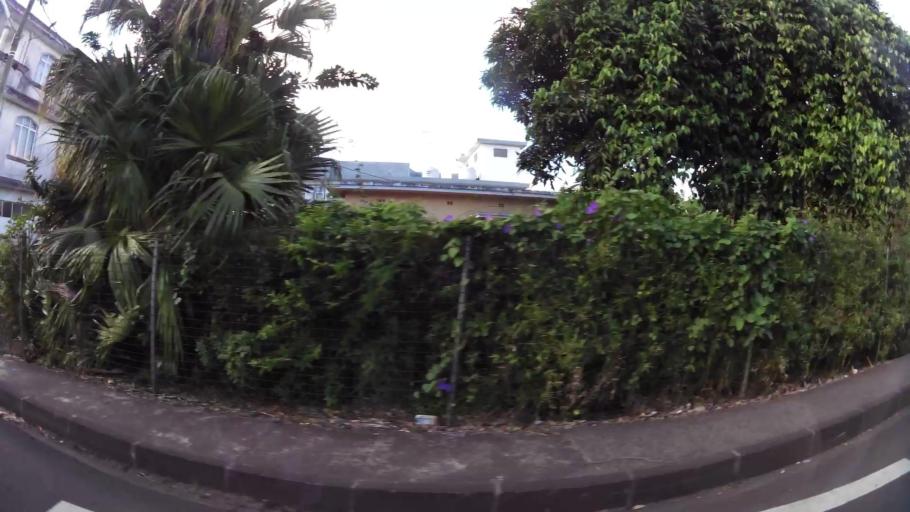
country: MU
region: Plaines Wilhems
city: Curepipe
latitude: -20.2873
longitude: 57.5086
